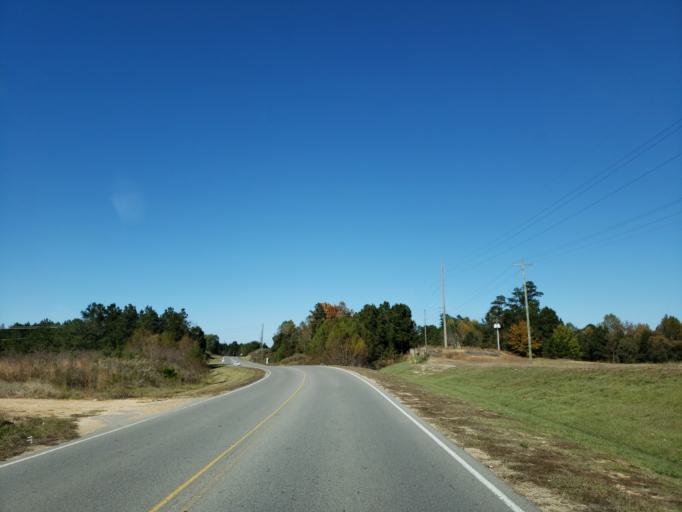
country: US
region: Mississippi
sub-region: Lamar County
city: West Hattiesburg
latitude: 31.3233
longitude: -89.3991
